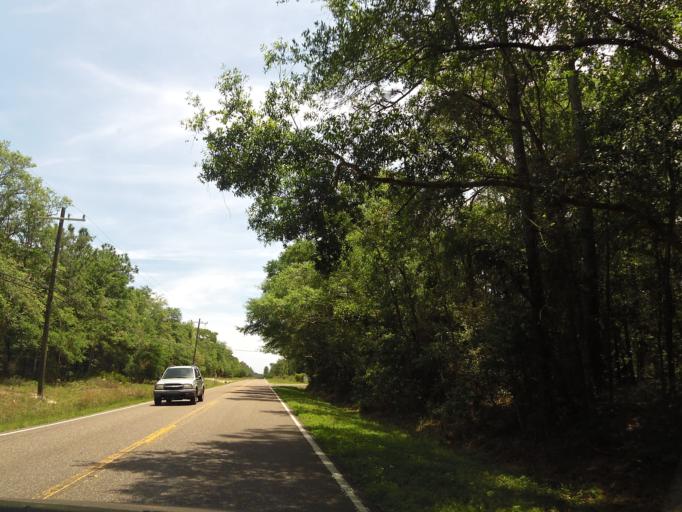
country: US
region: Florida
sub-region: Duval County
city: Atlantic Beach
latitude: 30.4584
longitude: -81.5123
